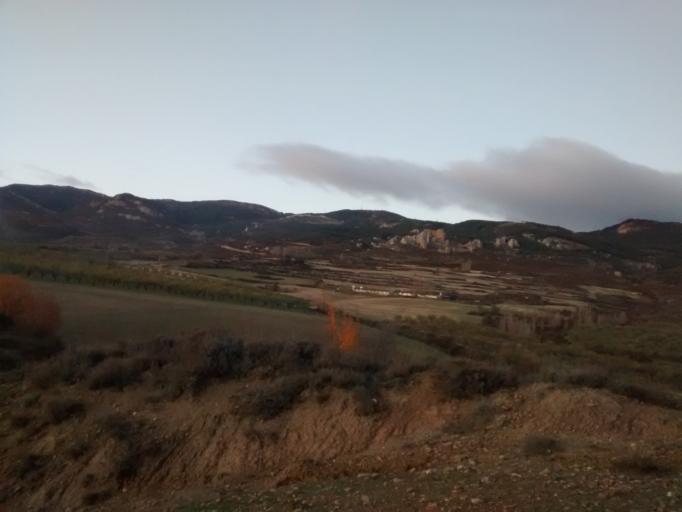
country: ES
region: Aragon
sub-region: Provincia de Huesca
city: Loarre
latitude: 42.3110
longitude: -0.6127
